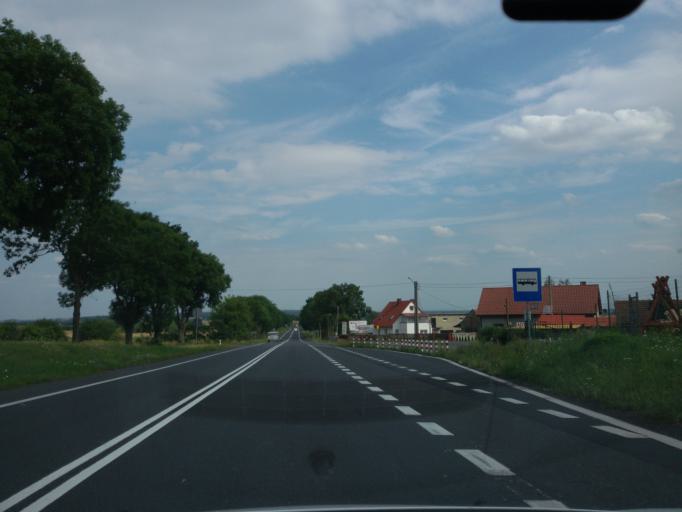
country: PL
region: Lower Silesian Voivodeship
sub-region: Powiat polkowicki
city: Gaworzyce
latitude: 51.6351
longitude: 15.8942
